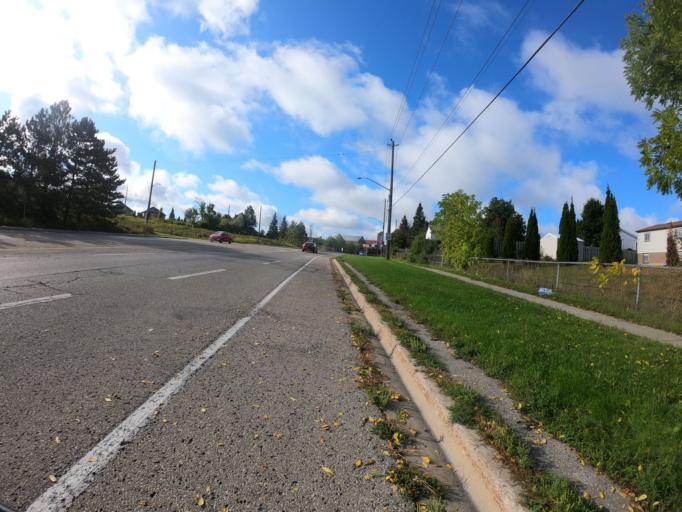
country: CA
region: Ontario
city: Waterloo
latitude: 43.4428
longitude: -80.5460
